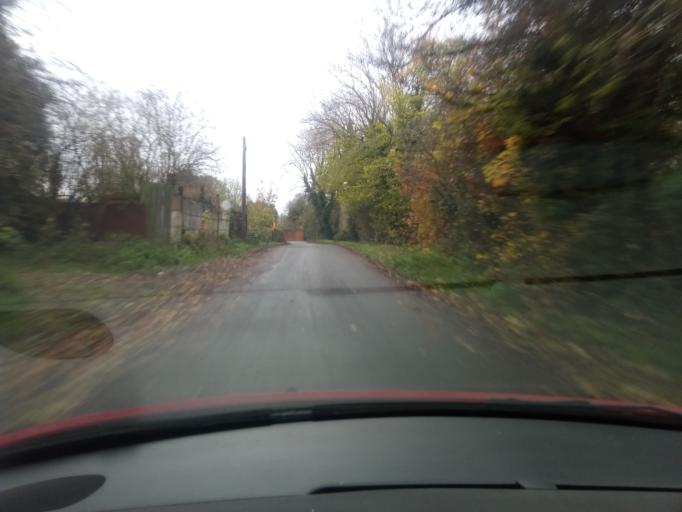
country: GB
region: England
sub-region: Derbyshire
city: Melbourne
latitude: 52.8680
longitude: -1.4248
